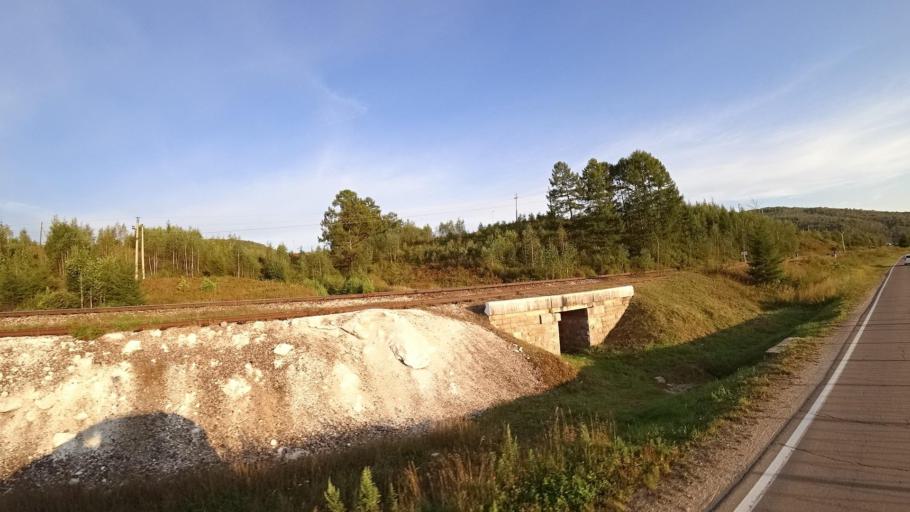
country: RU
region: Jewish Autonomous Oblast
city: Kul'dur
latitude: 49.2015
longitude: 131.6371
